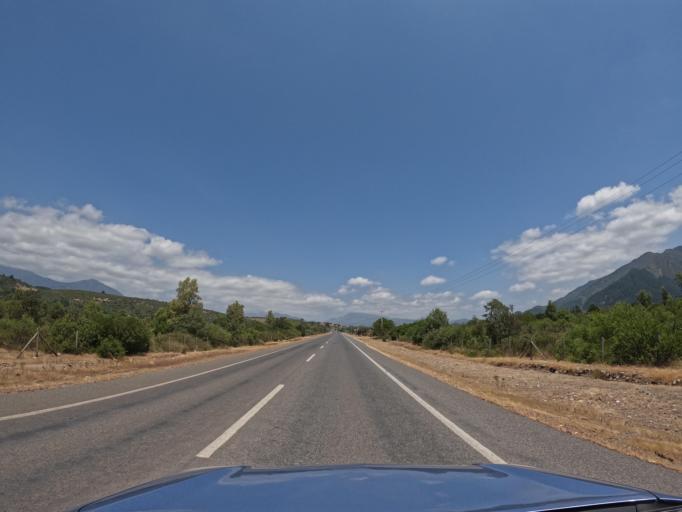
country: CL
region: Maule
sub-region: Provincia de Curico
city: Molina
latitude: -35.1731
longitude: -71.1251
